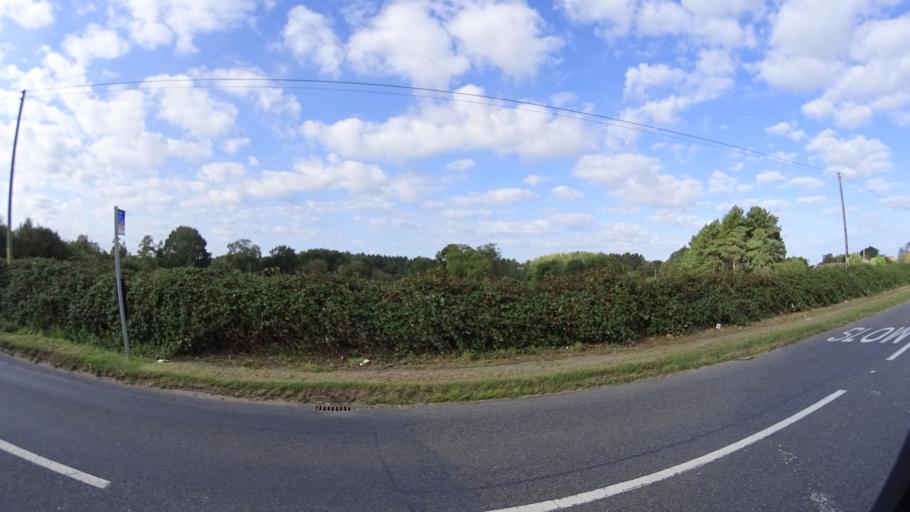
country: GB
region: England
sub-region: Dorset
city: Lytchett Matravers
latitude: 50.7618
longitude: -2.0567
